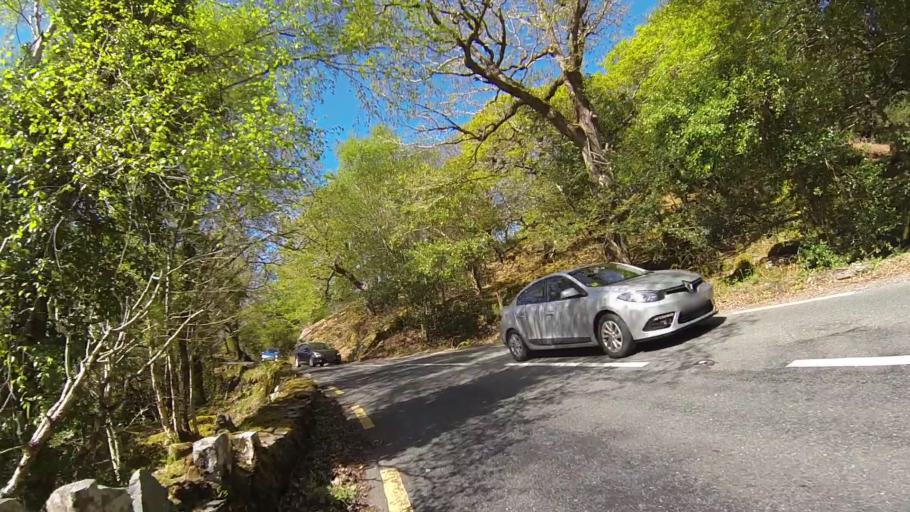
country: IE
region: Munster
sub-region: Ciarrai
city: Cill Airne
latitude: 51.9789
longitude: -9.5737
